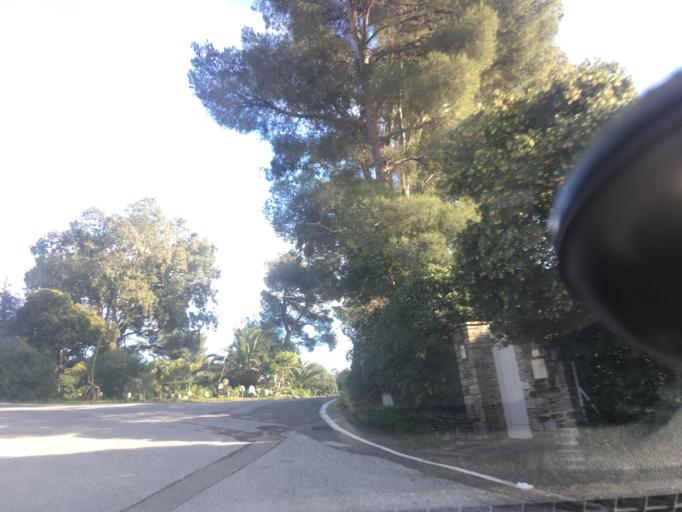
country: FR
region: Provence-Alpes-Cote d'Azur
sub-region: Departement du Var
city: Cavalaire-sur-Mer
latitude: 43.1576
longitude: 6.4772
